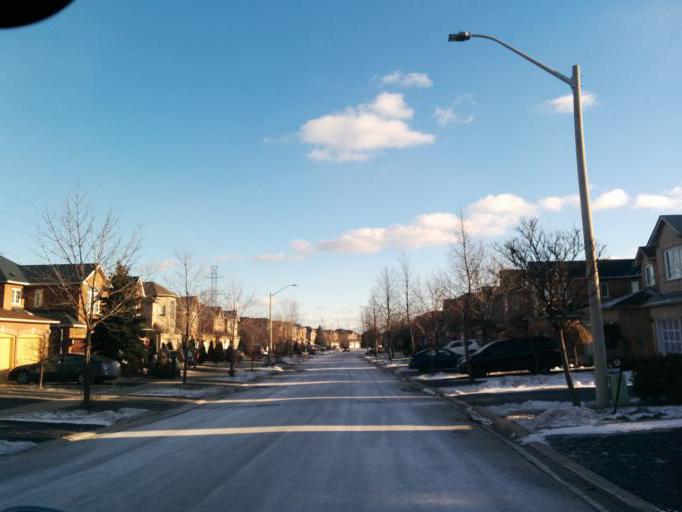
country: CA
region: Ontario
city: Mississauga
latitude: 43.6265
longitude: -79.6504
